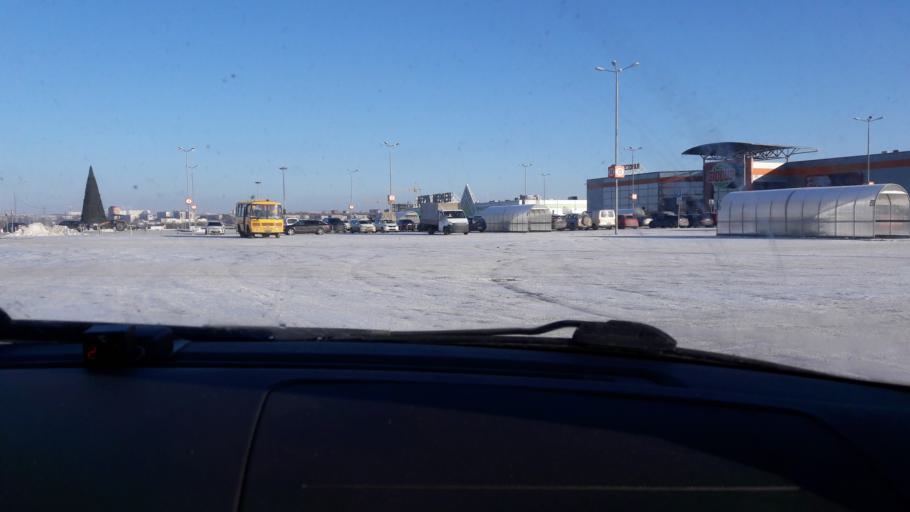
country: RU
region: Tula
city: Tula
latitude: 54.1764
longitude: 37.6449
